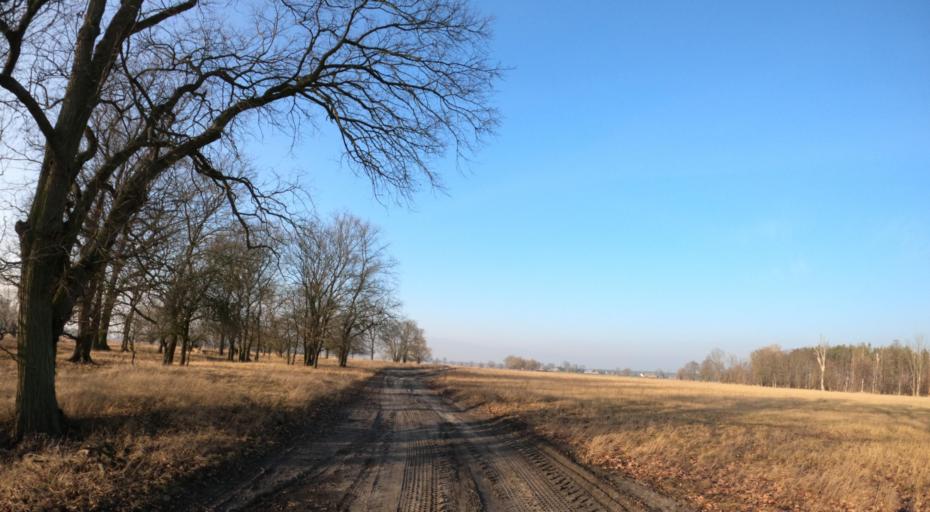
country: DE
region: Brandenburg
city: Zechin
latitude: 52.6547
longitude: 14.5059
